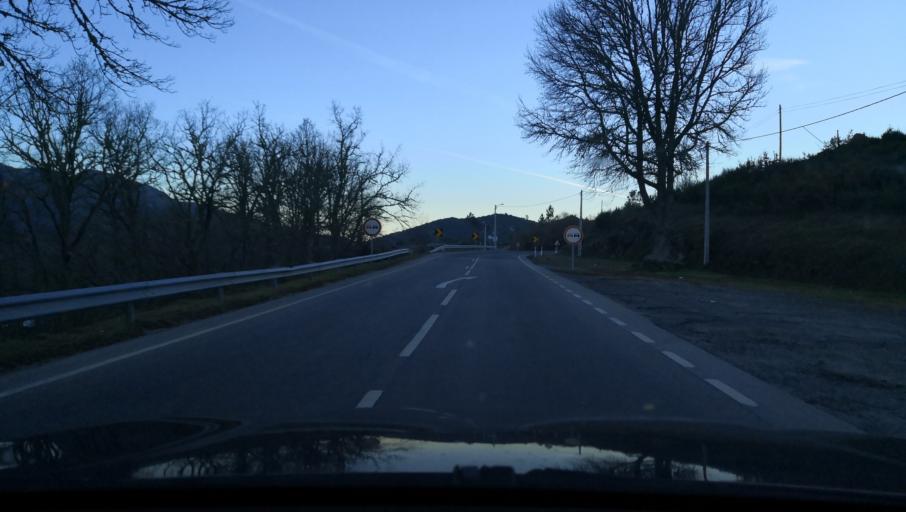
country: PT
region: Vila Real
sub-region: Vila Pouca de Aguiar
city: Vila Pouca de Aguiar
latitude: 41.4190
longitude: -7.6850
